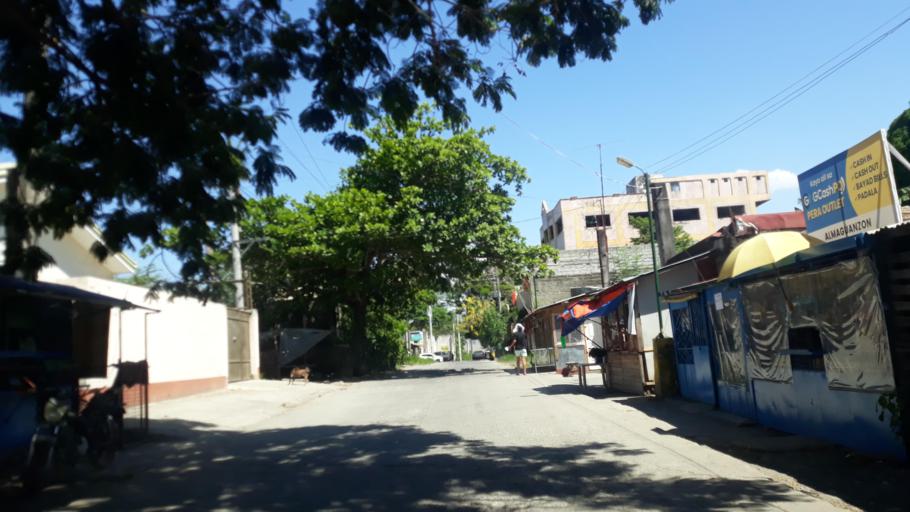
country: PH
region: Calabarzon
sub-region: Province of Cavite
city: Manggahan
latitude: 14.2997
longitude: 120.9166
